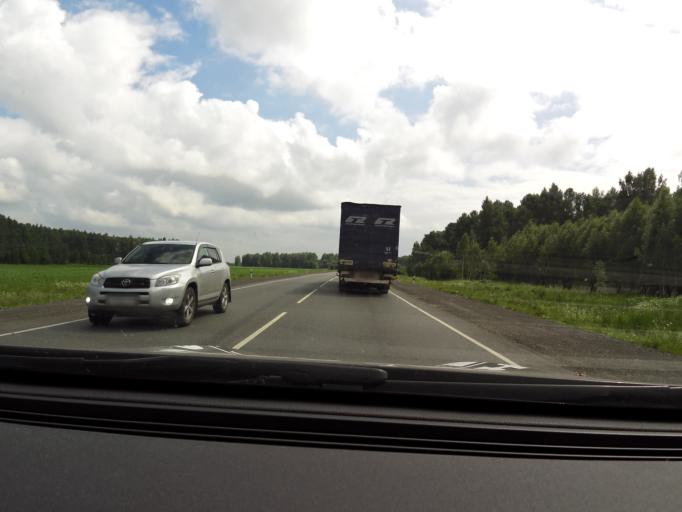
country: RU
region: Perm
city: Ust'-Kishert'
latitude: 57.1718
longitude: 57.1437
